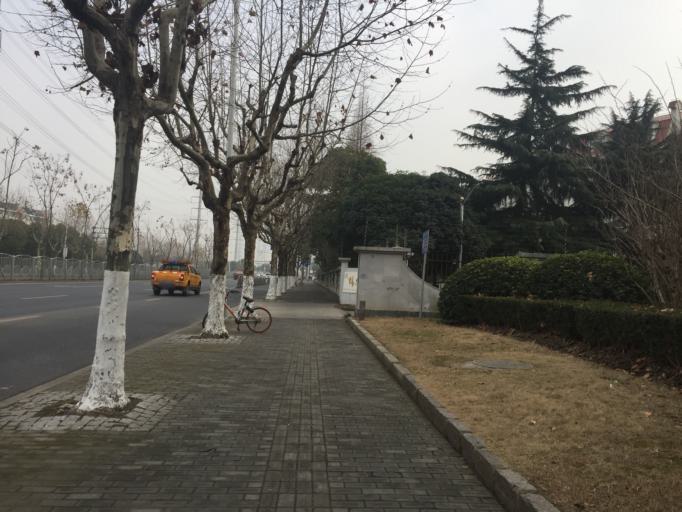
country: CN
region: Shanghai Shi
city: Huamu
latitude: 31.1895
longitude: 121.5330
